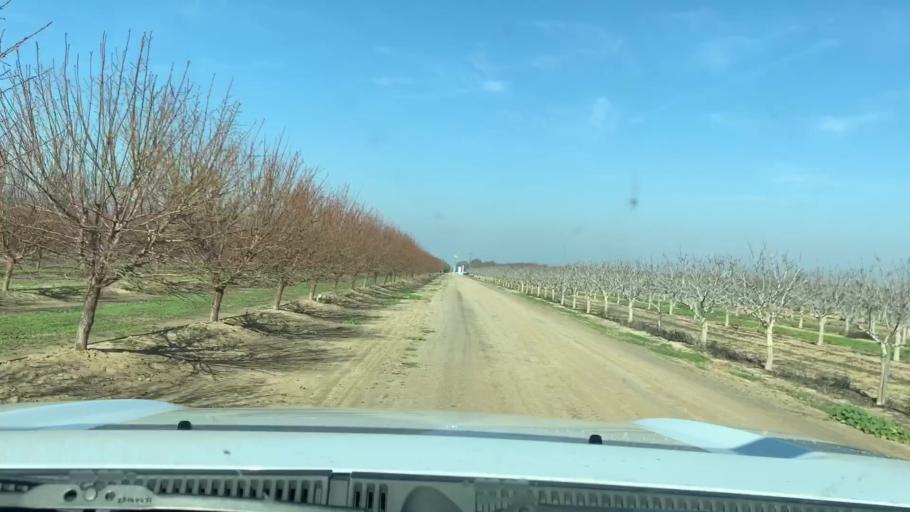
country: US
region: California
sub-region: Kern County
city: Lost Hills
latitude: 35.6127
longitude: -119.5358
